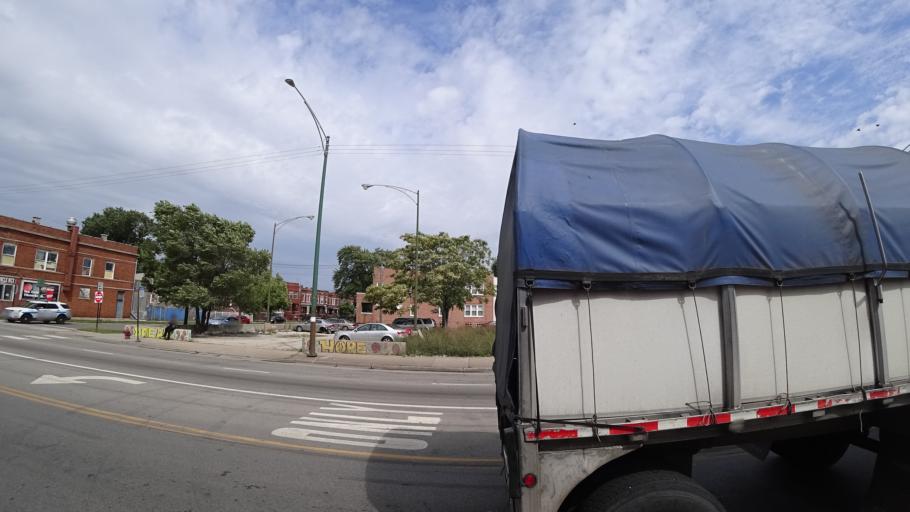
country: US
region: Illinois
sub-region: Cook County
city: Cicero
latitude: 41.8740
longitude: -87.7450
